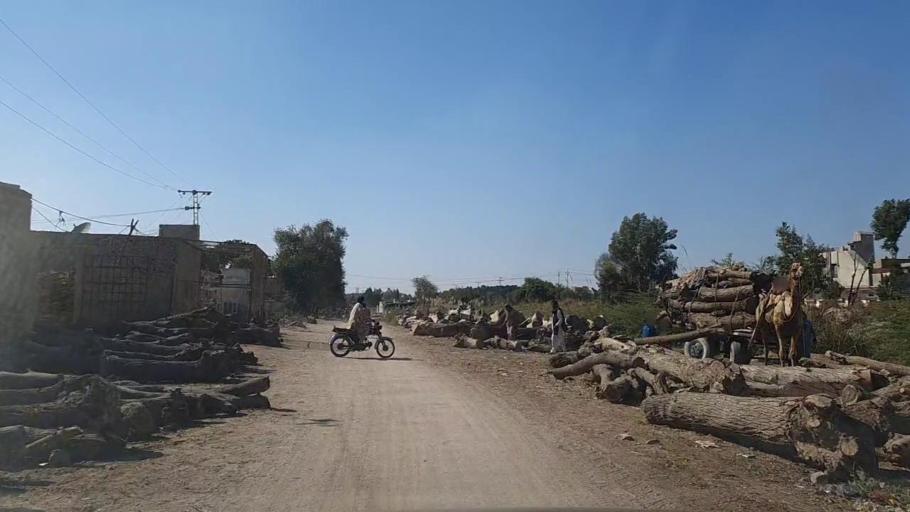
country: PK
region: Sindh
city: Nawabshah
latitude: 26.2441
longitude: 68.4270
